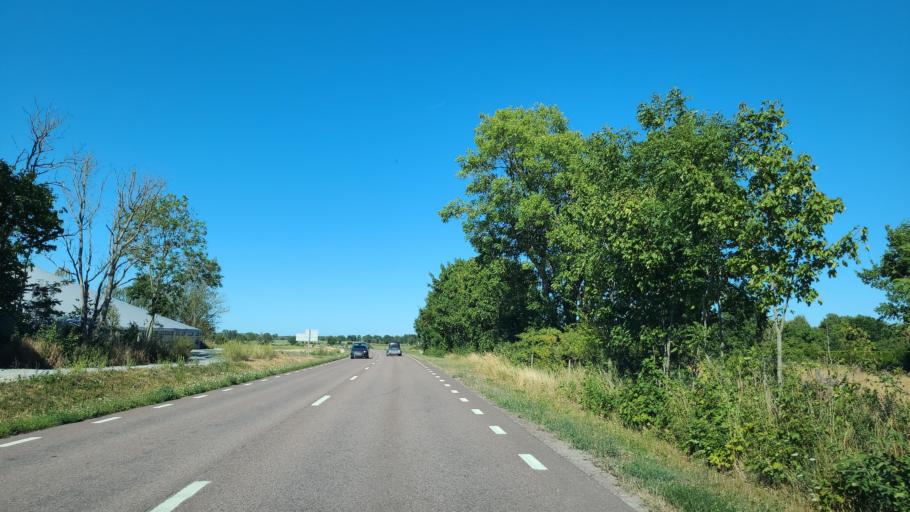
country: SE
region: Kalmar
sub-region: Borgholms Kommun
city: Borgholm
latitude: 57.1214
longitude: 16.9647
